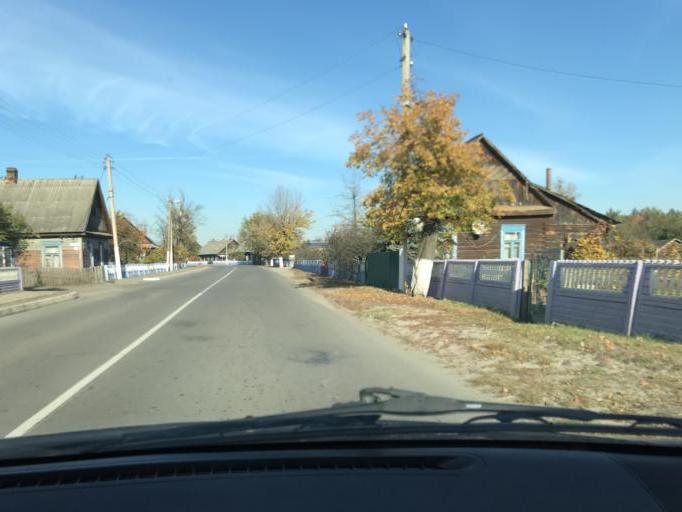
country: BY
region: Brest
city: Mikashevichy
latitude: 52.2265
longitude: 27.4602
